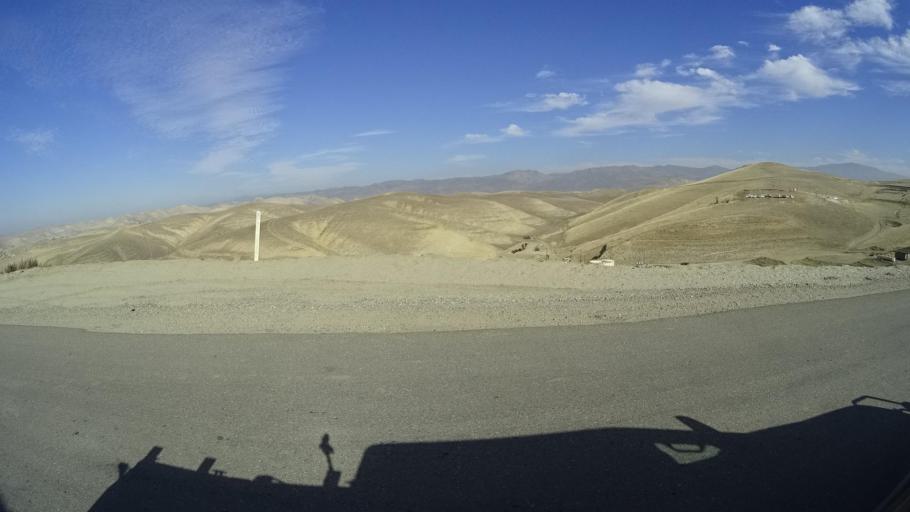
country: US
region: California
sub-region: Kern County
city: Oildale
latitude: 35.4879
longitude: -118.8880
